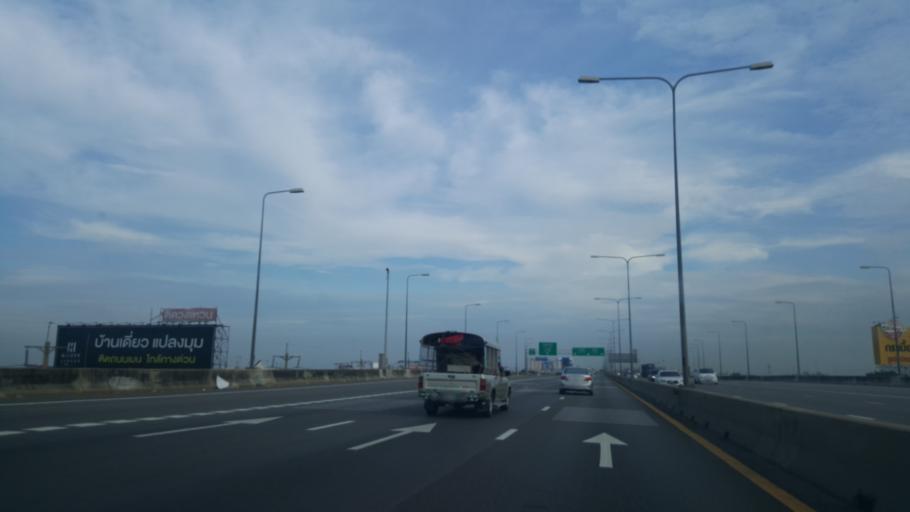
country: TH
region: Bangkok
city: Bang Na
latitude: 13.6420
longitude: 100.6962
